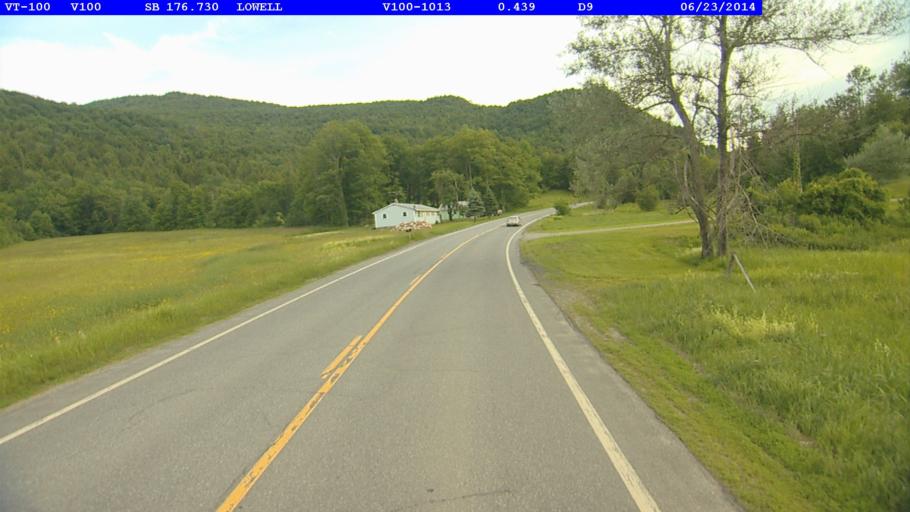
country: US
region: Vermont
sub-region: Lamoille County
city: Hyde Park
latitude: 44.7452
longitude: -72.4613
